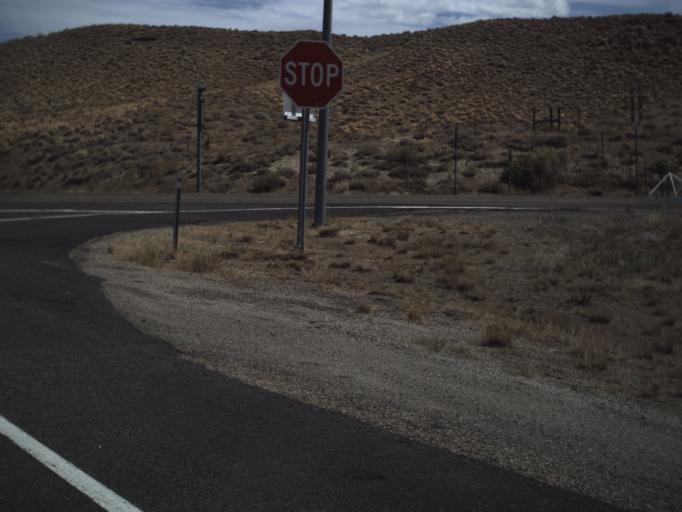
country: US
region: Utah
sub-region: Grand County
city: Moab
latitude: 38.9610
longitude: -109.7225
